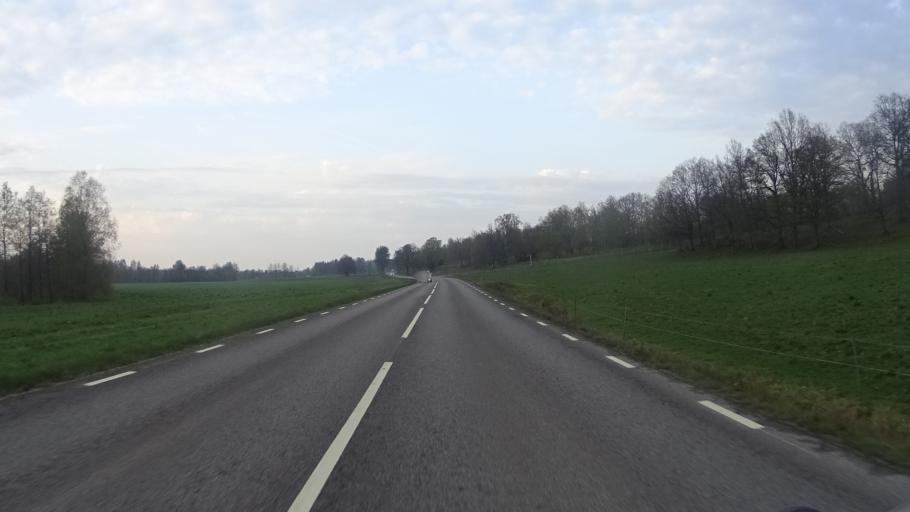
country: SE
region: Kronoberg
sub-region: Ljungby Kommun
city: Ljungby
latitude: 56.8443
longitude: 13.9721
